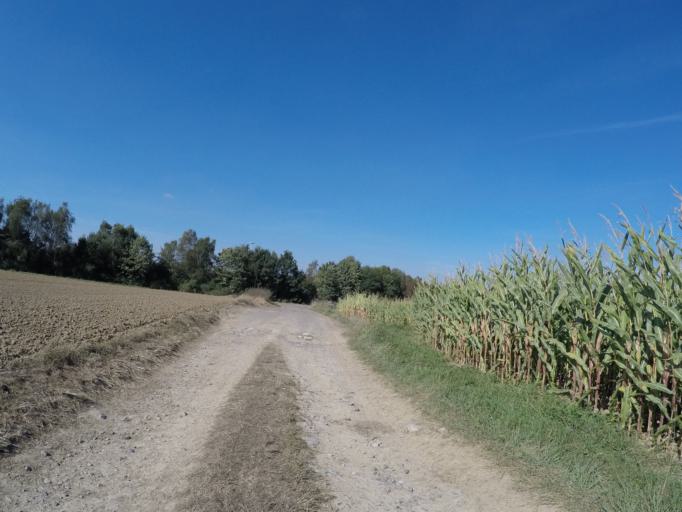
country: BE
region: Wallonia
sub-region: Province de Namur
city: Assesse
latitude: 50.3074
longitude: 5.0209
